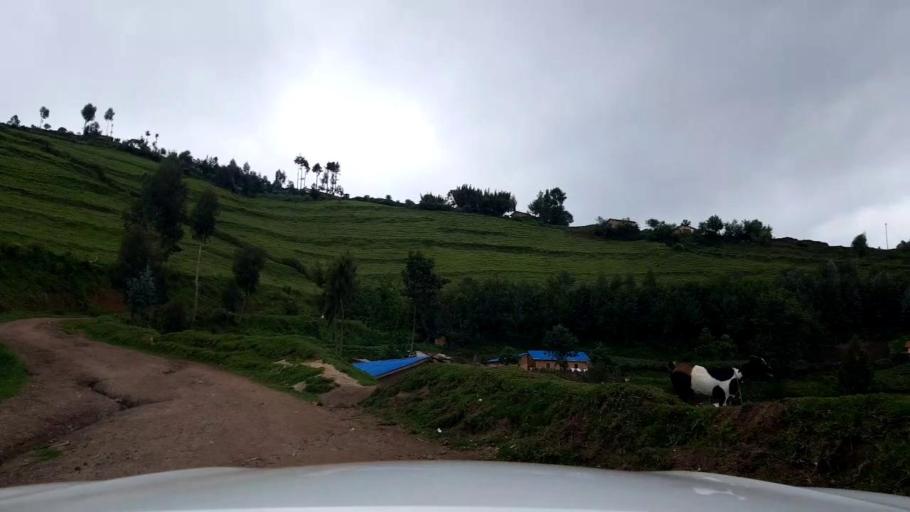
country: RW
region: Western Province
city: Gisenyi
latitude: -1.6745
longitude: 29.4120
